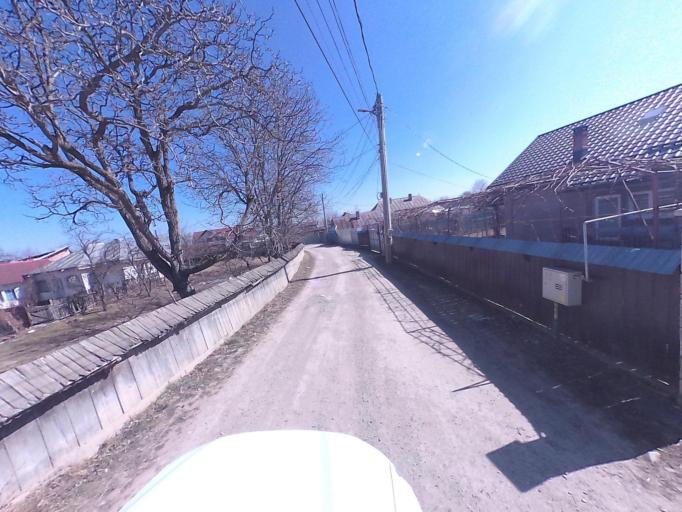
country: RO
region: Neamt
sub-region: Oras Targu Neamt
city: Humulesti
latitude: 47.1959
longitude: 26.3562
